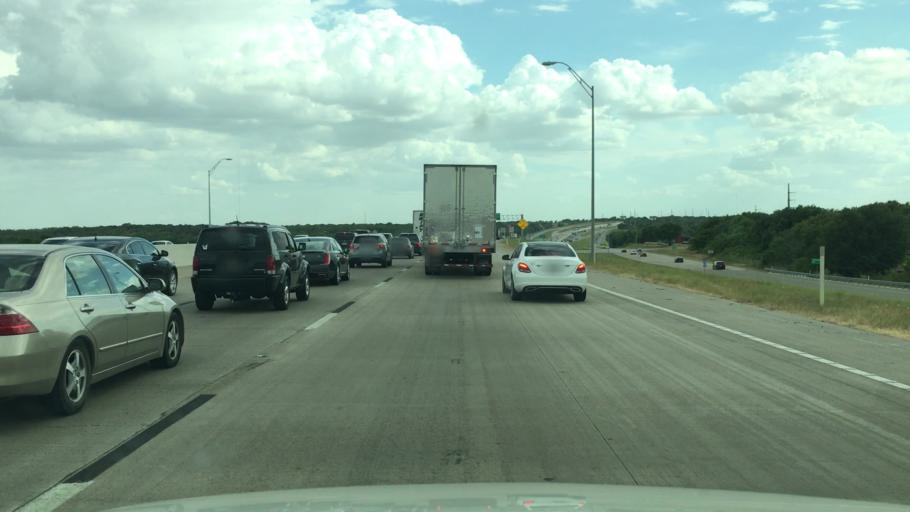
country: US
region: Texas
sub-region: McLennan County
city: Lorena
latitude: 31.3414
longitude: -97.2220
